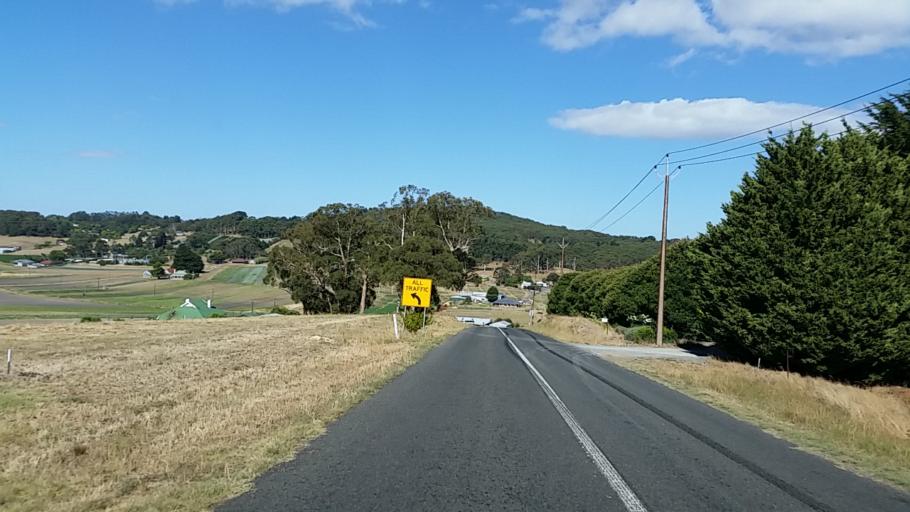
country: AU
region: South Australia
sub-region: Adelaide Hills
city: Bridgewater
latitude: -34.9680
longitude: 138.7314
